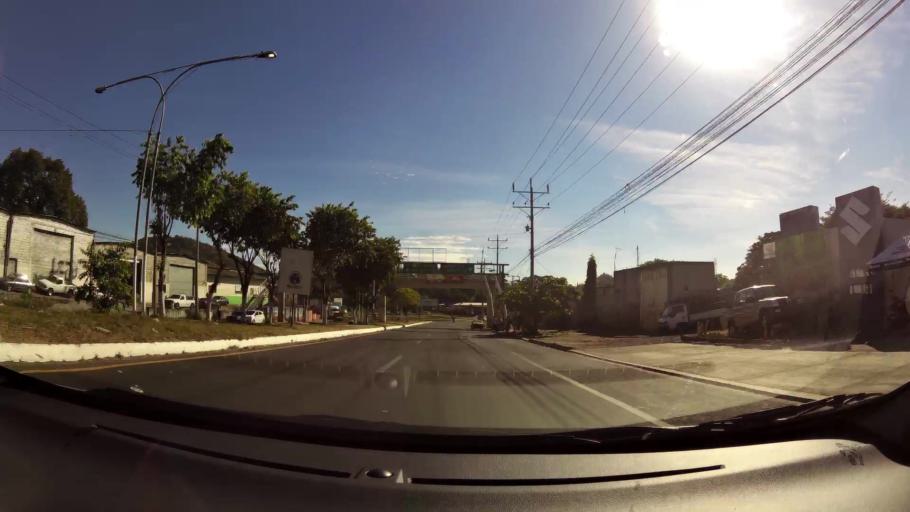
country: SV
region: Santa Ana
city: Santa Ana
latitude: 13.9850
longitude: -89.5485
